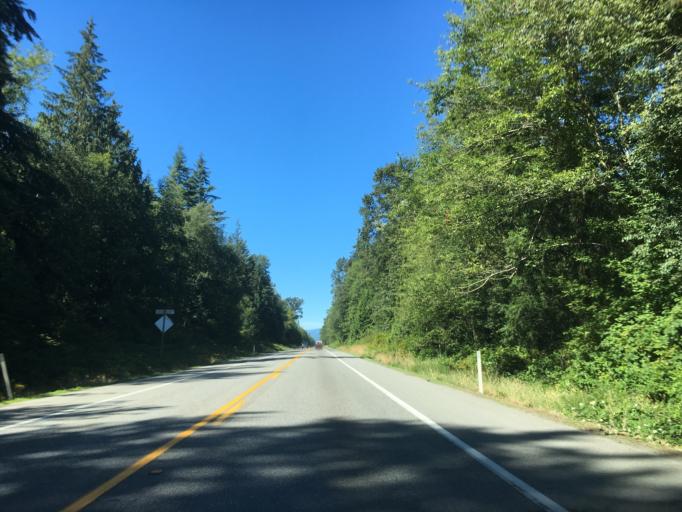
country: US
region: Washington
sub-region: Snohomish County
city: Sisco Heights
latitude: 48.1164
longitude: -122.1124
